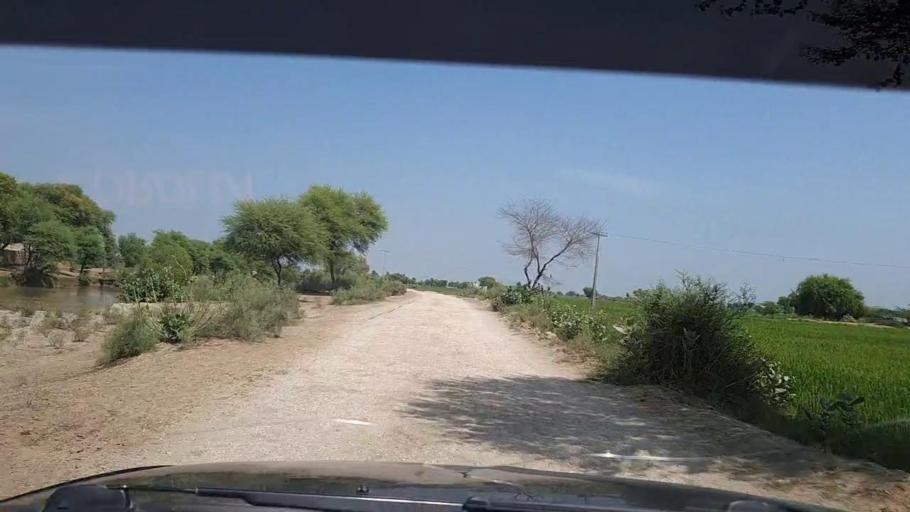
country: PK
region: Sindh
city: Tangwani
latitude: 28.2351
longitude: 68.9884
